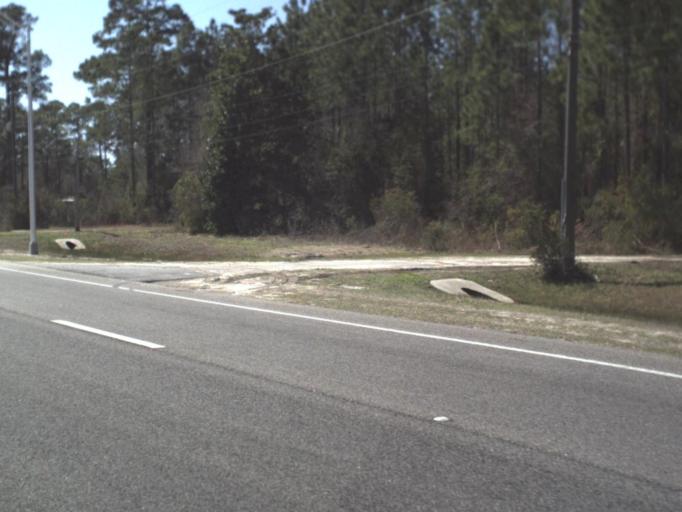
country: US
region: Florida
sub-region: Bay County
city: Laguna Beach
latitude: 30.3002
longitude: -85.8528
